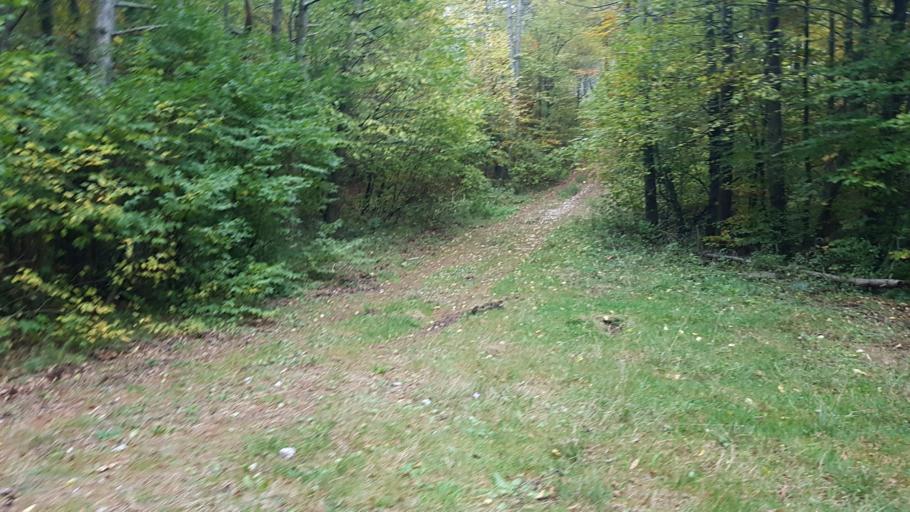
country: HR
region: Istarska
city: Buzet
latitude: 45.4028
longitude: 14.1354
